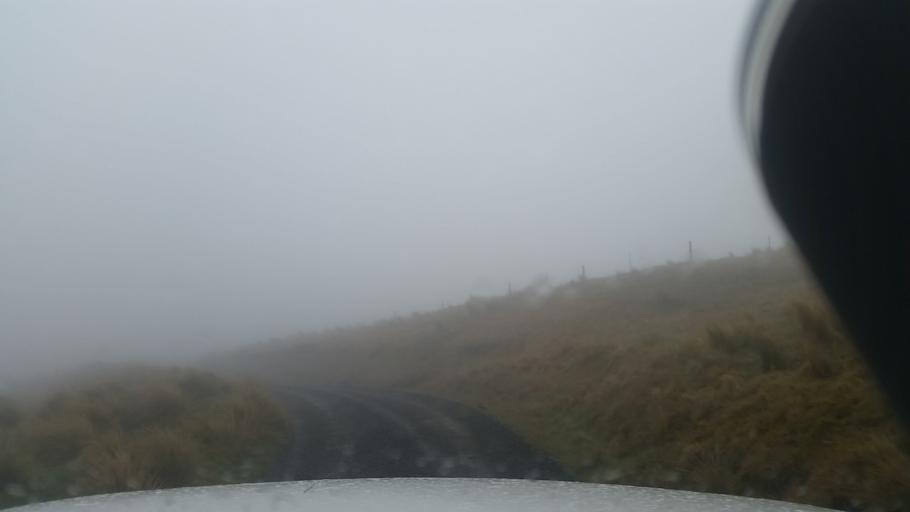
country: NZ
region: Canterbury
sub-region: Christchurch City
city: Christchurch
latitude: -43.8709
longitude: 172.9072
